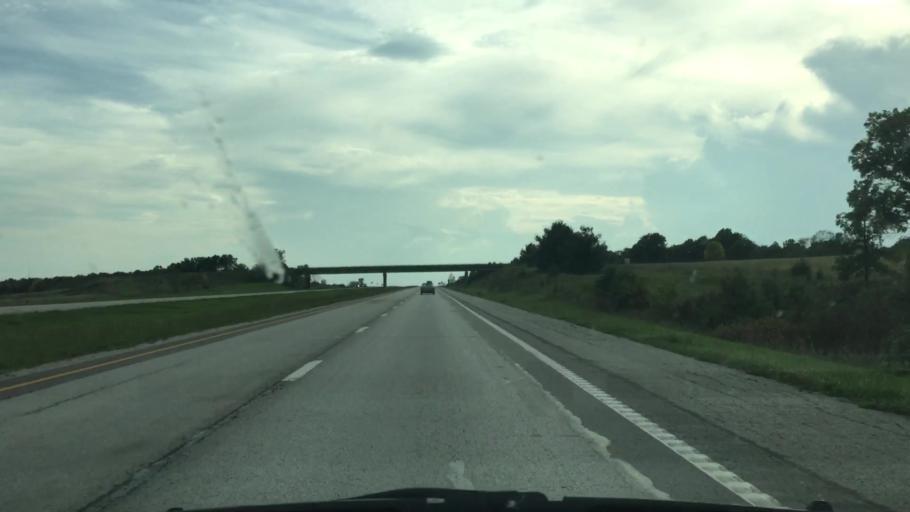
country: US
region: Missouri
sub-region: Harrison County
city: Bethany
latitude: 40.1401
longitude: -94.0442
